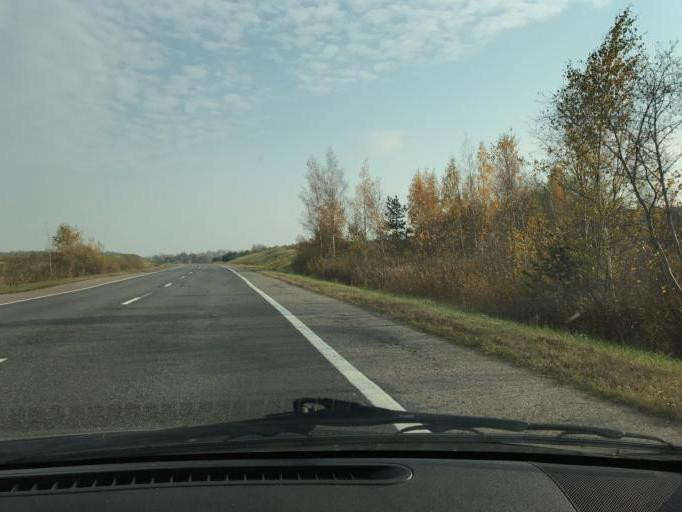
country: BY
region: Vitebsk
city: Lyepyel'
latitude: 54.9891
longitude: 28.8971
